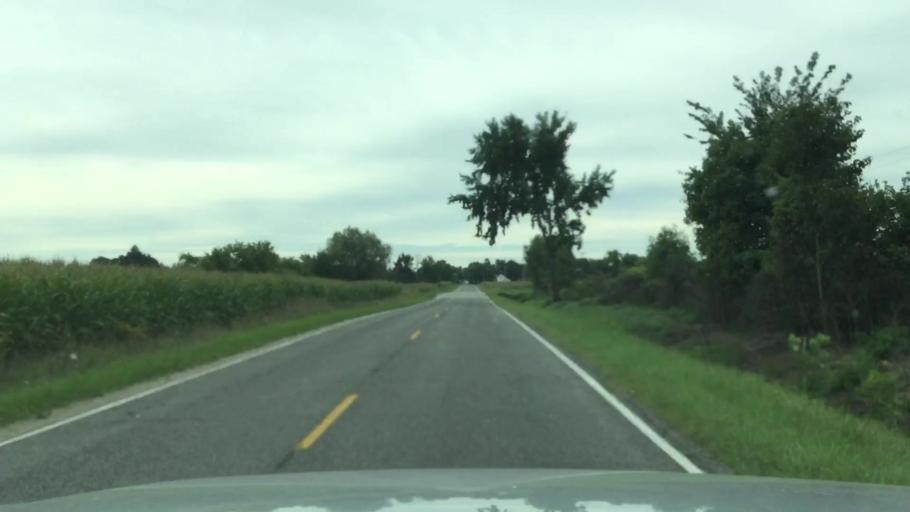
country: US
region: Michigan
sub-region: Genesee County
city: Flushing
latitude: 43.0649
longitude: -83.9876
